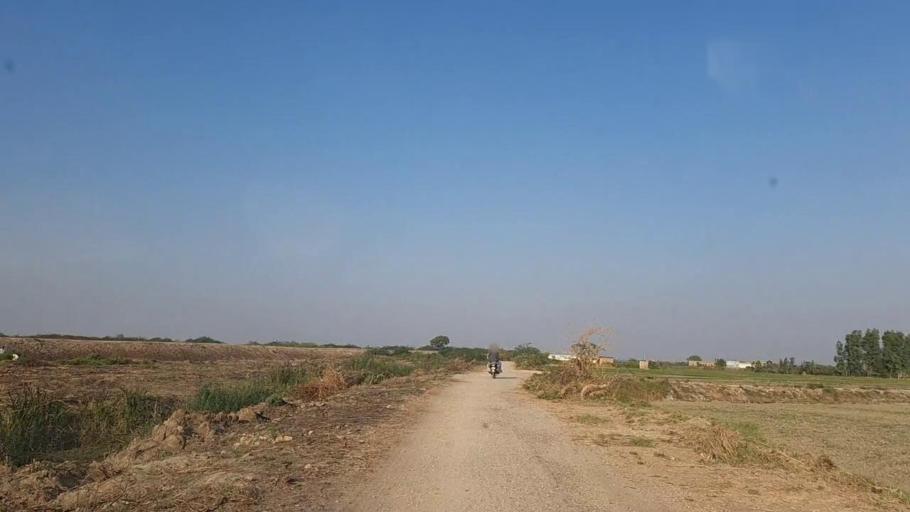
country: PK
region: Sindh
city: Thatta
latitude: 24.7238
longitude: 67.9474
